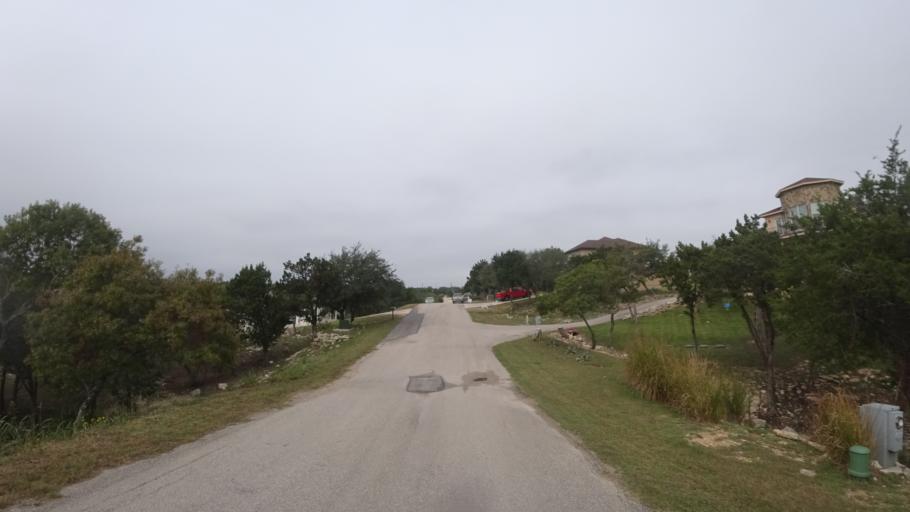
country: US
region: Texas
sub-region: Travis County
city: Hudson Bend
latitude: 30.3932
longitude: -97.9218
